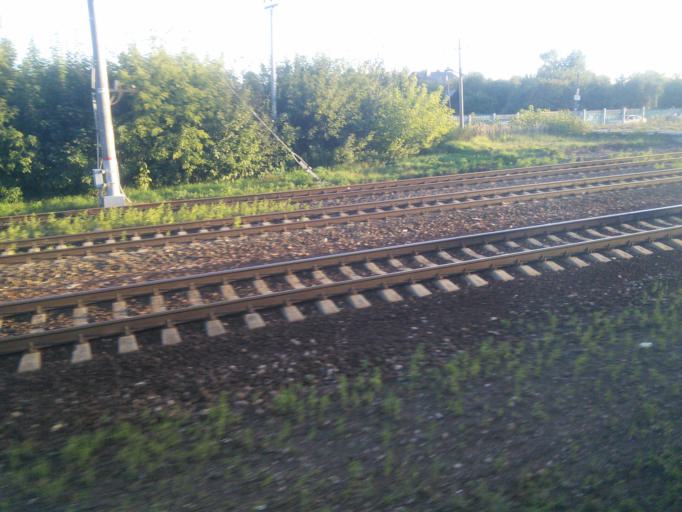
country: RU
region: Moskovskaya
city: Imeni Vorovskogo
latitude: 55.7210
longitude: 38.3505
